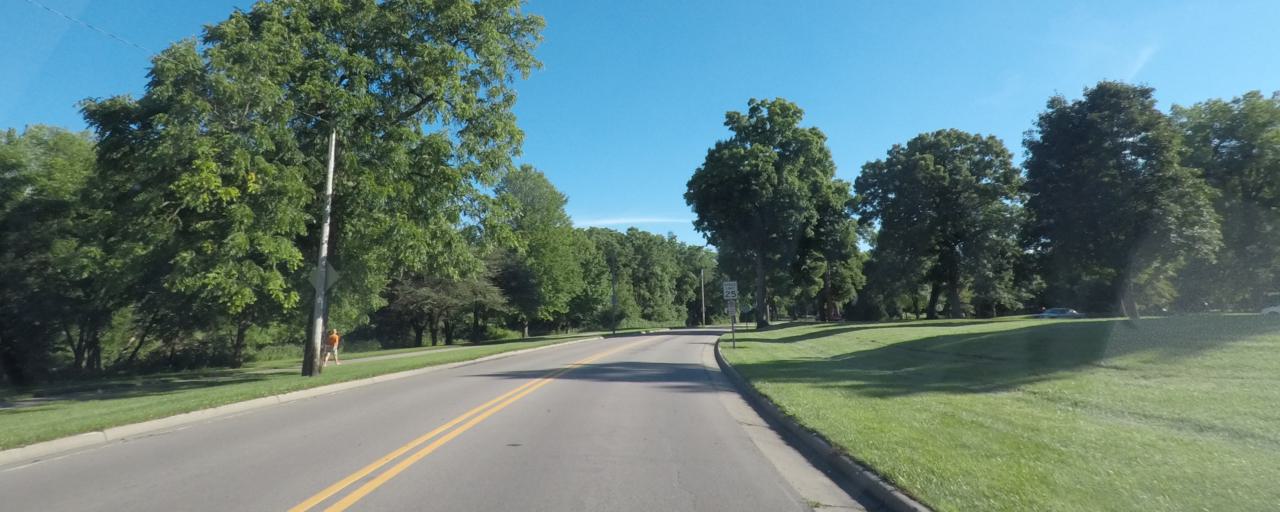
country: US
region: Wisconsin
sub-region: Rock County
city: Janesville
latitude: 42.6784
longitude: -88.9903
